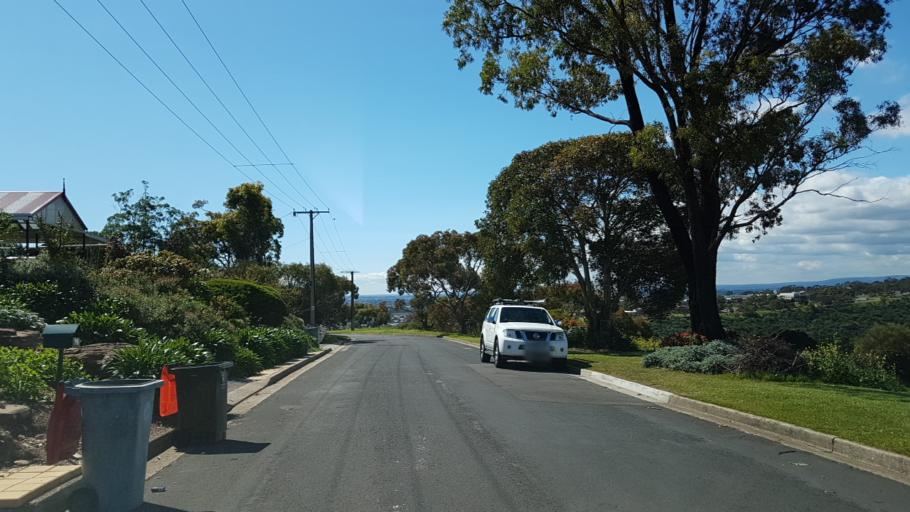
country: AU
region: South Australia
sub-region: Onkaparinga
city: Bedford Park
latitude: -35.0371
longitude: 138.5674
